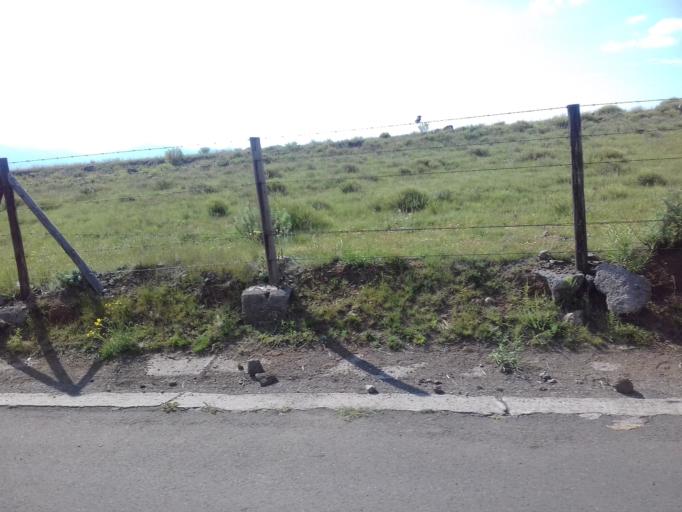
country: LS
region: Thaba-Tseka
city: Thaba-Tseka
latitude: -29.5195
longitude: 28.6179
